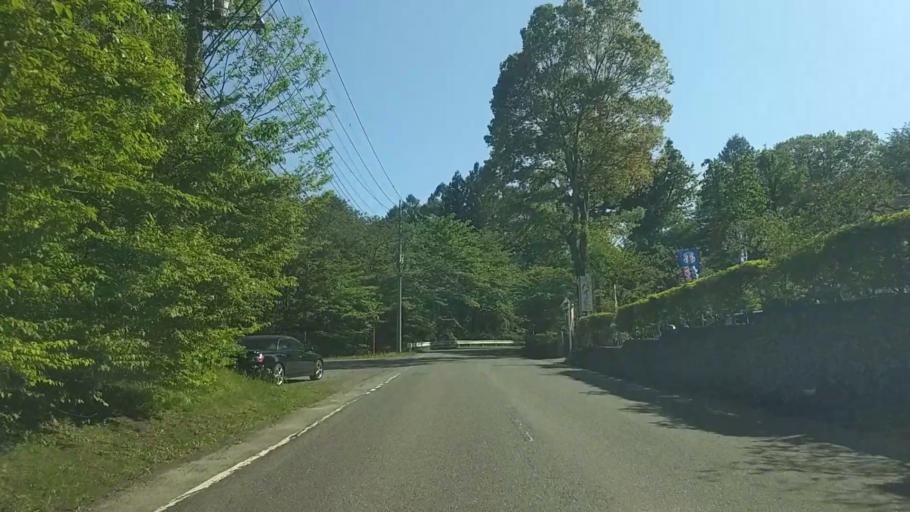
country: JP
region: Yamanashi
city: Nirasaki
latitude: 35.8869
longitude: 138.3835
